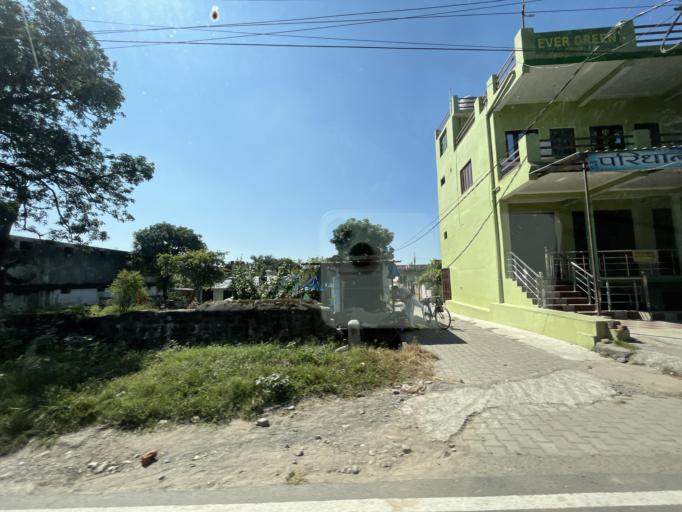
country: IN
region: Uttarakhand
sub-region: Naini Tal
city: Kaladhungi
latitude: 29.2869
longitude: 79.3454
